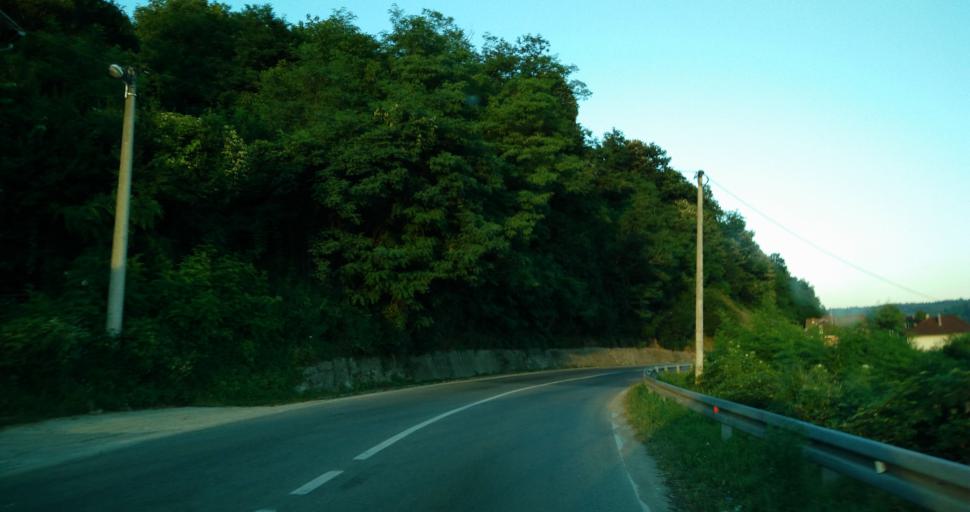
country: BA
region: Republika Srpska
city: Bosanski Novi
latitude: 45.0480
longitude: 16.3911
